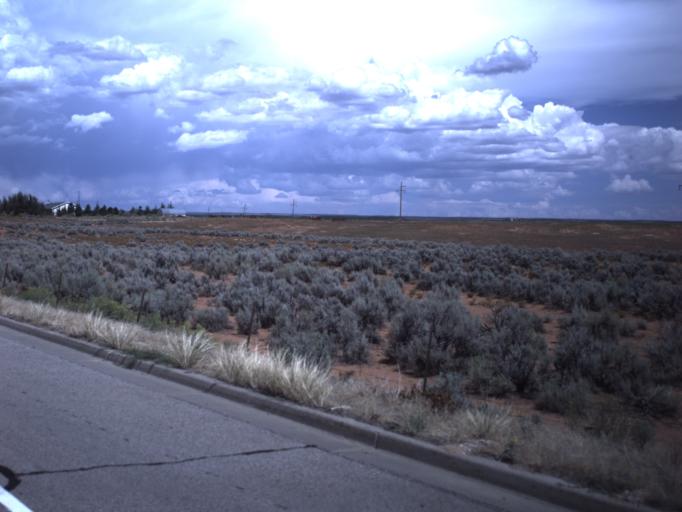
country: US
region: Utah
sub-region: San Juan County
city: Blanding
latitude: 37.6012
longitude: -109.4786
